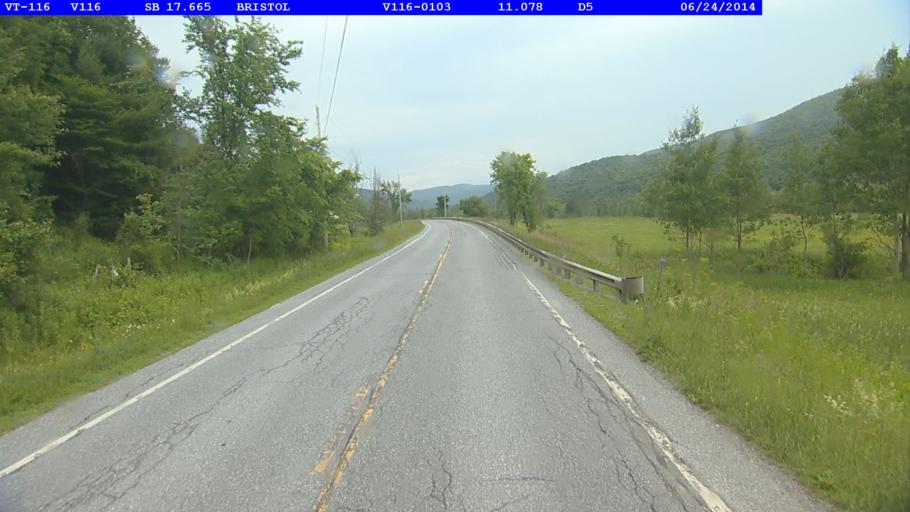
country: US
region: Vermont
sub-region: Addison County
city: Bristol
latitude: 44.1686
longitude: -73.0557
